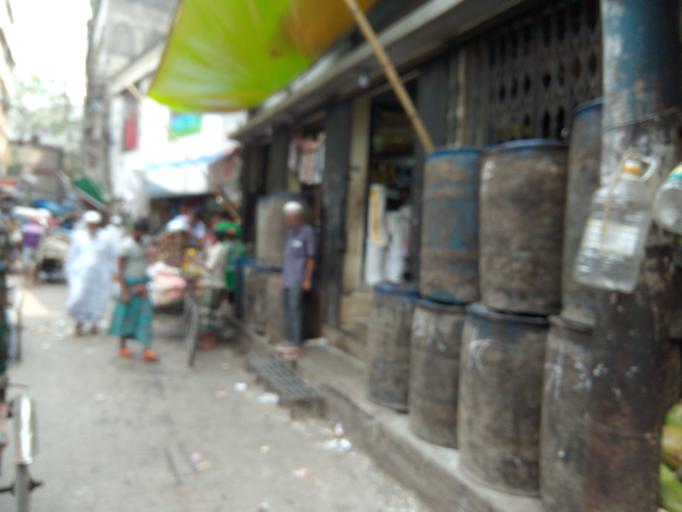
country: BD
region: Dhaka
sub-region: Dhaka
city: Dhaka
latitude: 23.7217
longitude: 90.4138
